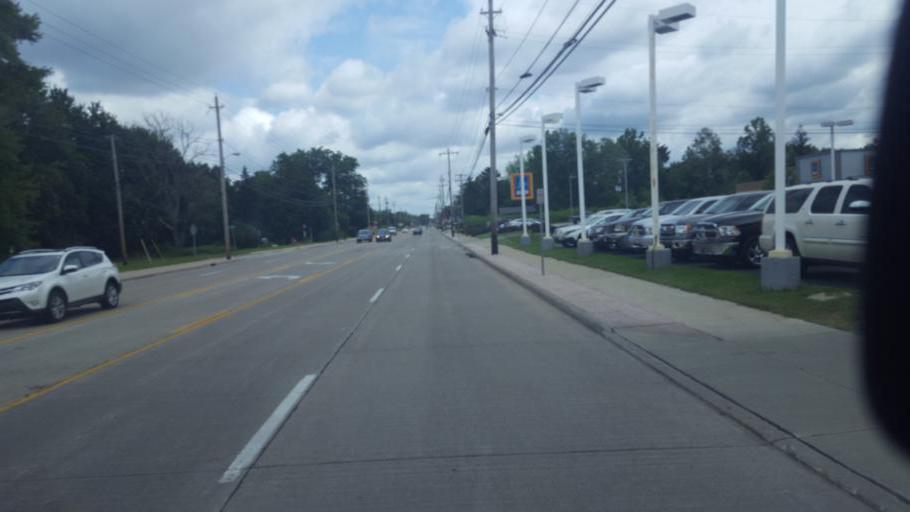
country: US
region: Ohio
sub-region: Lake County
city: Mentor
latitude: 41.6879
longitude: -81.2899
